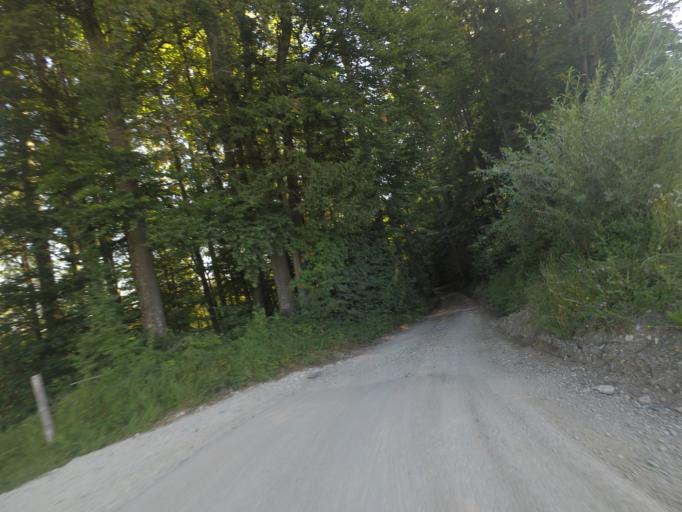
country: AT
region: Salzburg
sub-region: Politischer Bezirk Salzburg-Umgebung
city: Eugendorf
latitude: 47.8649
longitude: 13.0990
